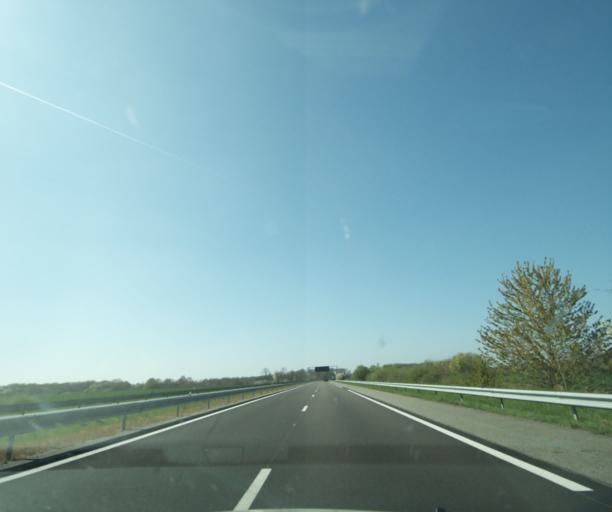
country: FR
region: Centre
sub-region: Departement du Loiret
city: Briare
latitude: 47.6353
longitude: 2.7772
